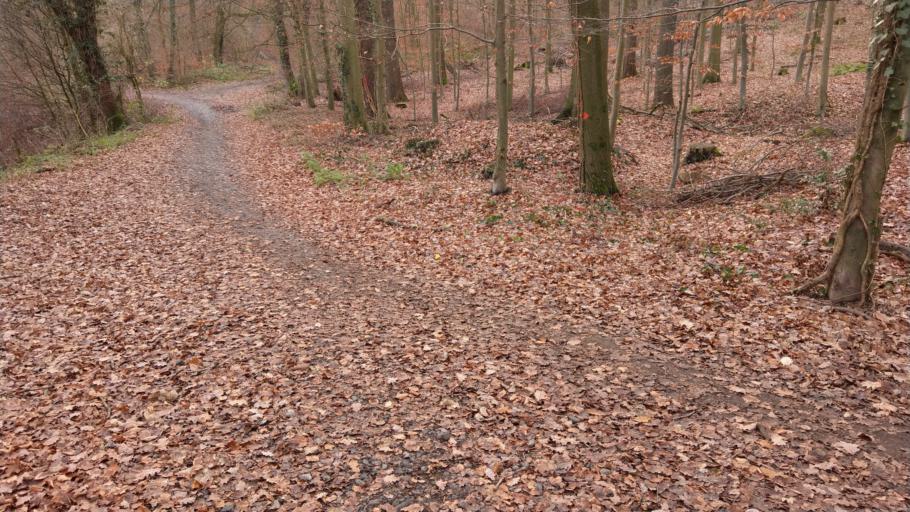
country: DE
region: North Rhine-Westphalia
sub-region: Regierungsbezirk Koln
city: Aachen
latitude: 50.7436
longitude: 6.0625
